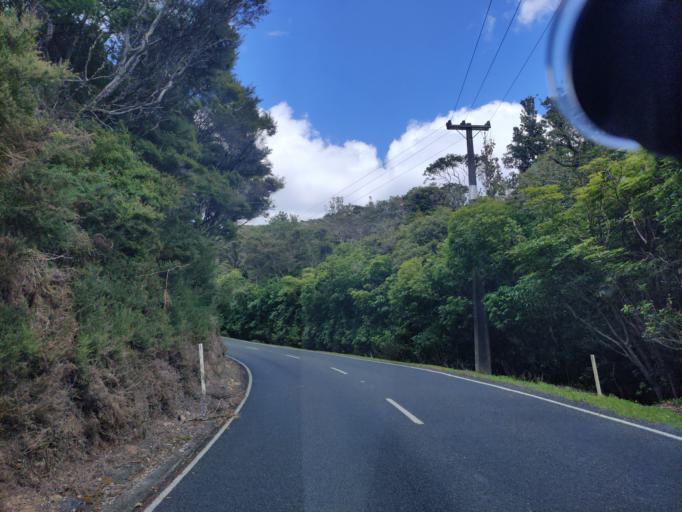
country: NZ
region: Northland
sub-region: Far North District
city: Paihia
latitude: -35.2600
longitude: 174.2209
